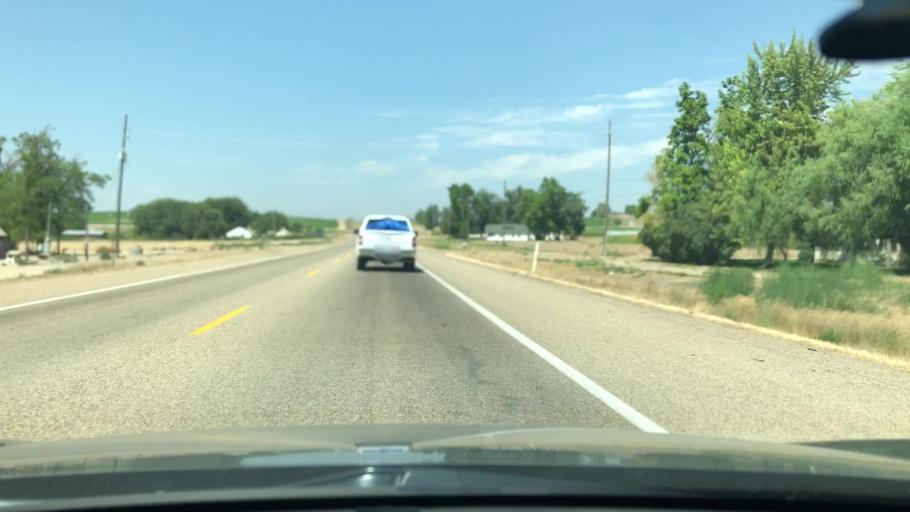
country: US
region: Idaho
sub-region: Canyon County
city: Parma
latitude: 43.8139
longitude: -116.9543
